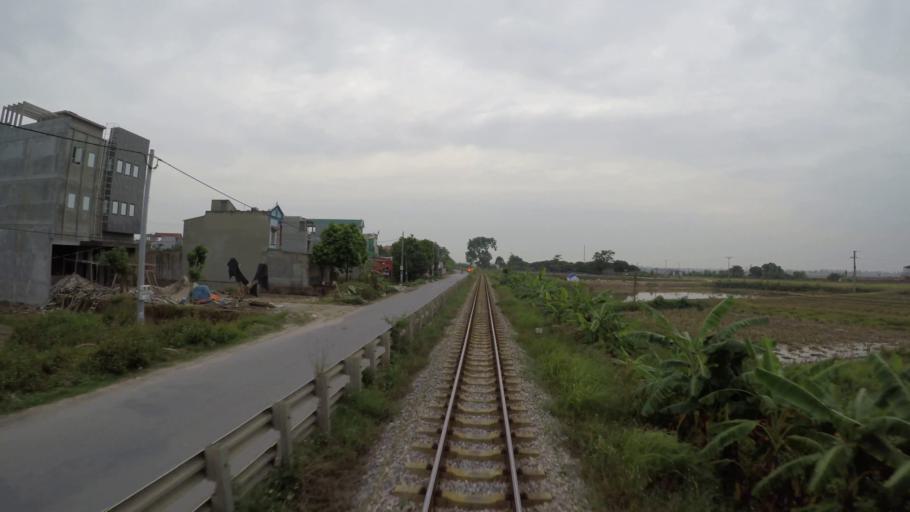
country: VN
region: Hung Yen
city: Ban Yen Nhan
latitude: 20.9698
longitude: 106.1021
